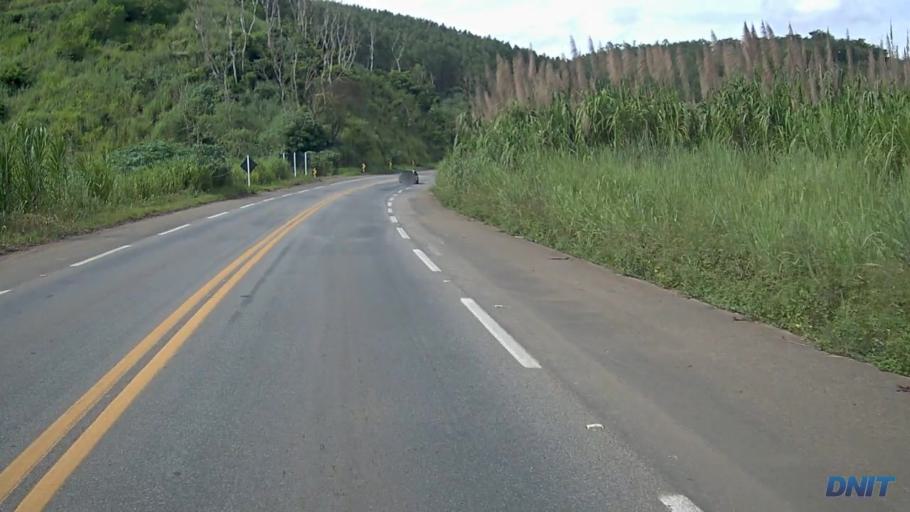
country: BR
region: Minas Gerais
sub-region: Ipaba
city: Ipaba
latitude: -19.3619
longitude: -42.4479
